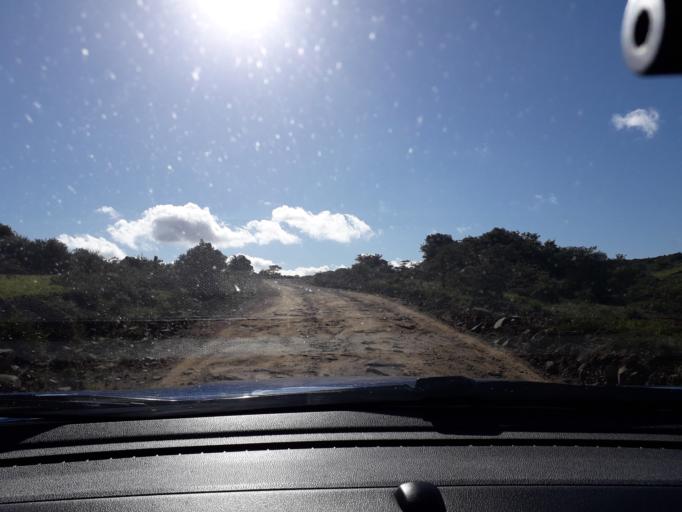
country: ZA
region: Eastern Cape
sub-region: Buffalo City Metropolitan Municipality
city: Bhisho
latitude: -33.1231
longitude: 27.4511
